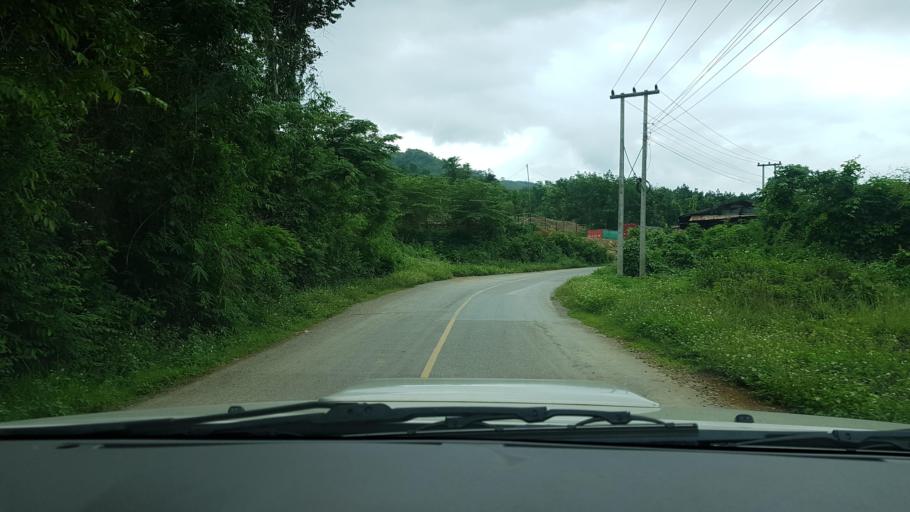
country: LA
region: Loungnamtha
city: Muang Nale
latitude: 20.2297
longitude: 101.5628
